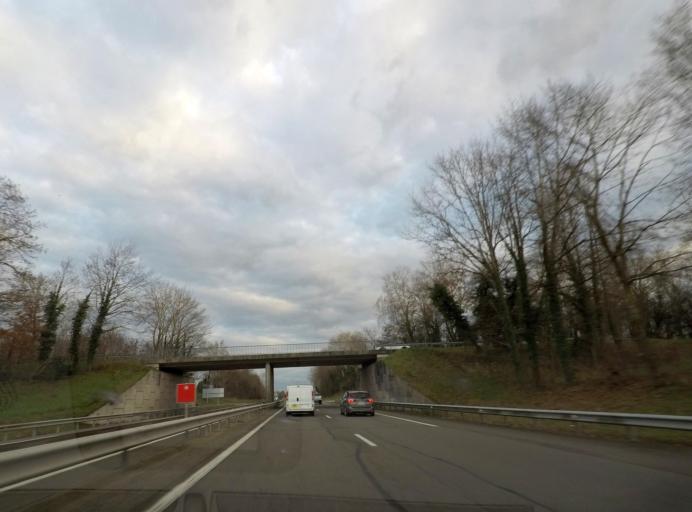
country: FR
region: Rhone-Alpes
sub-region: Departement de l'Ain
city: Crottet
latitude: 46.2925
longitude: 4.9143
